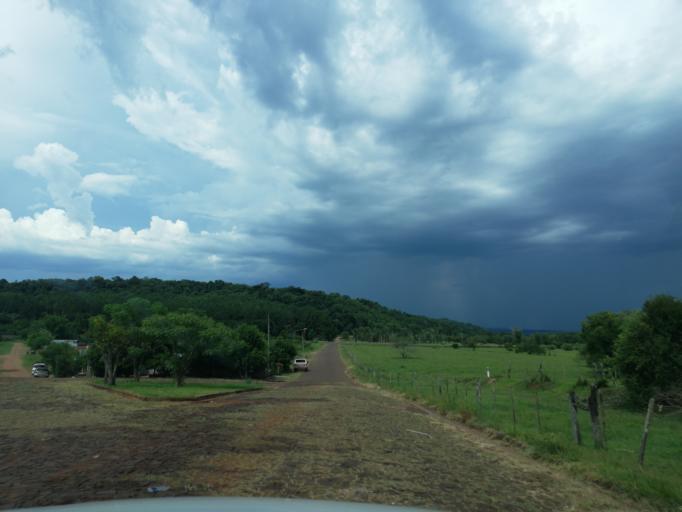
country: AR
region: Misiones
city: Cerro Azul
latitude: -27.5724
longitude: -55.5001
